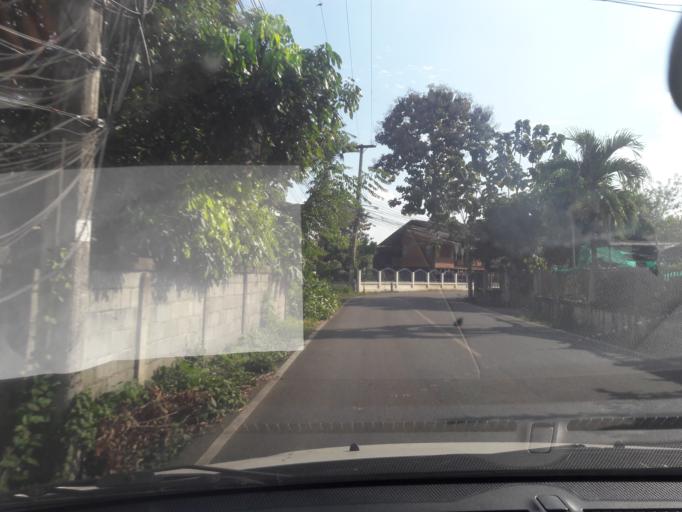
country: TH
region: Chiang Mai
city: San Kamphaeng
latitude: 18.7560
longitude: 99.1413
